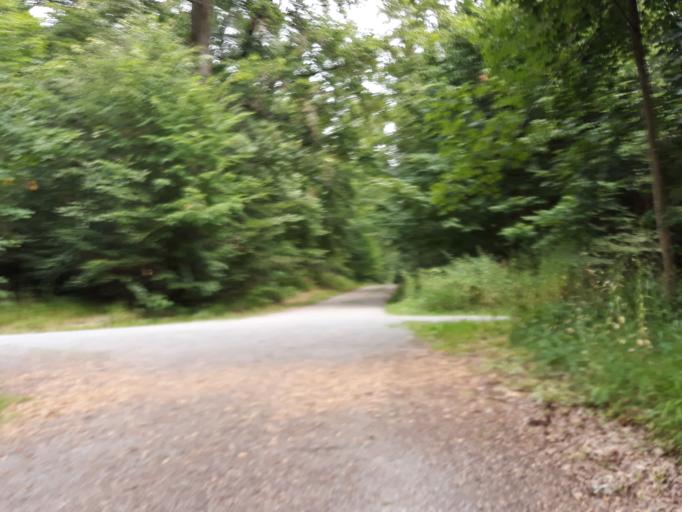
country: DE
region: Baden-Wuerttemberg
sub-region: Regierungsbezirk Stuttgart
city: Schonaich
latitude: 48.6720
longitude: 9.0463
